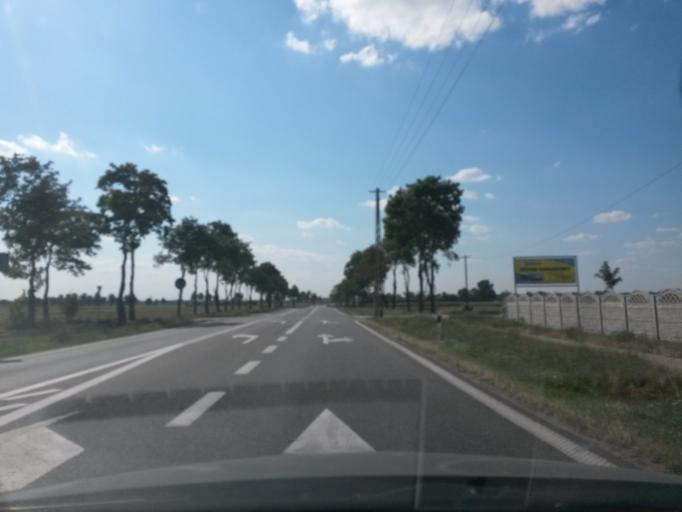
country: PL
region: Masovian Voivodeship
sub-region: Powiat plonski
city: Dzierzaznia
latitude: 52.6293
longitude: 20.1962
